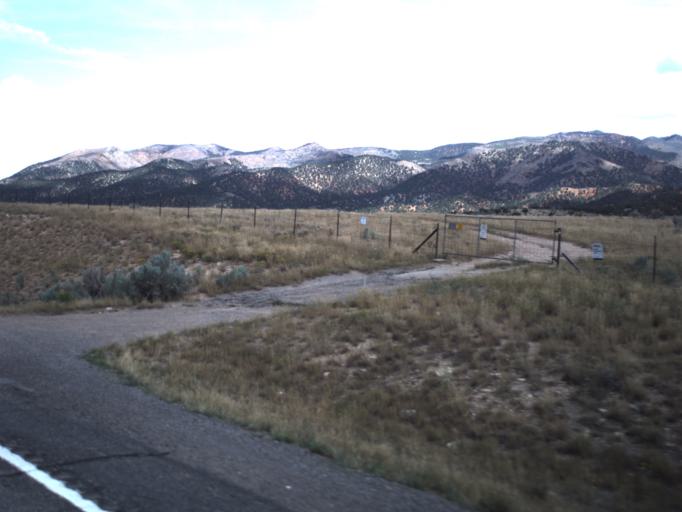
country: US
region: Utah
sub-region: Utah County
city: Woodland Hills
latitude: 39.8502
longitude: -111.5188
